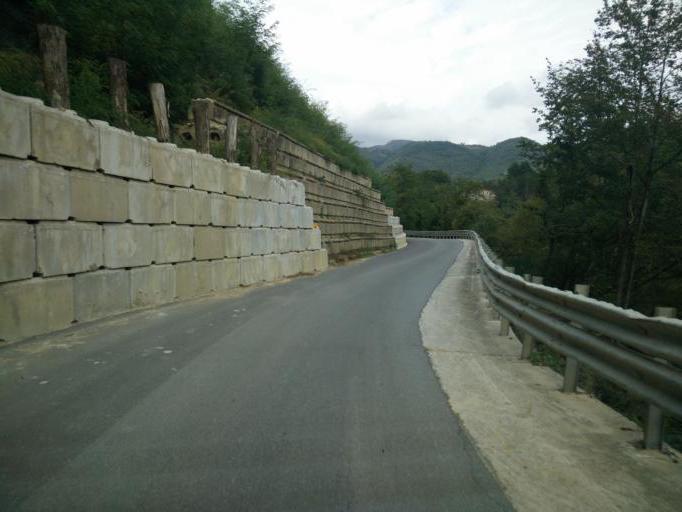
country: IT
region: Tuscany
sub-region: Provincia di Massa-Carrara
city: Casola in Lunigiana
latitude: 44.2168
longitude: 10.1935
